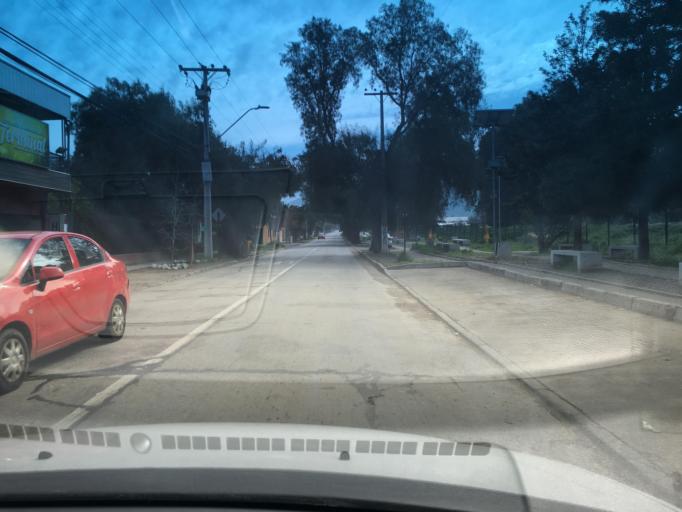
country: CL
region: Santiago Metropolitan
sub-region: Provincia de Chacabuco
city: Lampa
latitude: -33.0822
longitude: -70.9280
